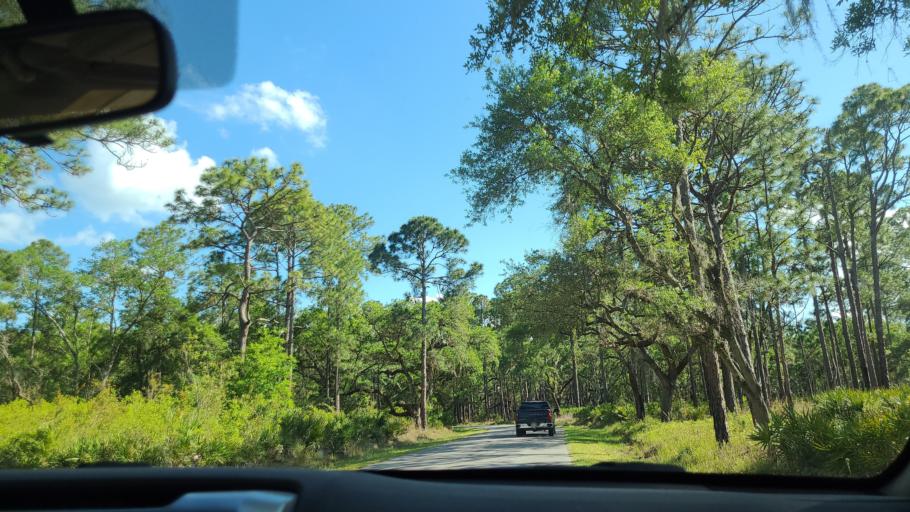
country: US
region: Florida
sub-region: Polk County
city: Babson Park
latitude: 27.9536
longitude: -81.3738
